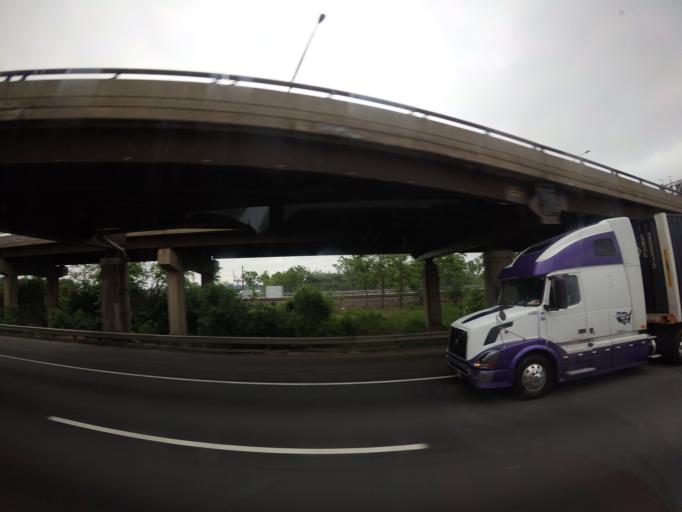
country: US
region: New Jersey
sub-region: Union County
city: Elizabeth
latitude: 40.6446
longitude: -74.2036
